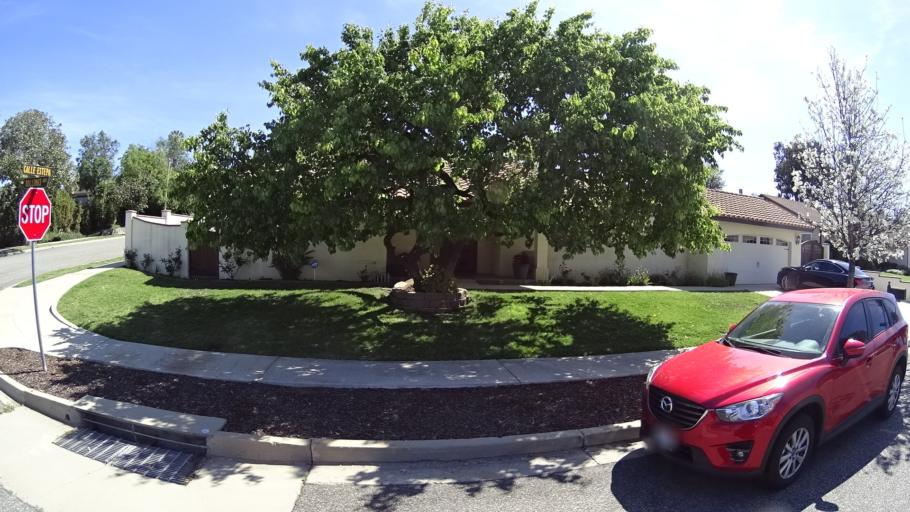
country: US
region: California
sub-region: Ventura County
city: Thousand Oaks
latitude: 34.2214
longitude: -118.8584
